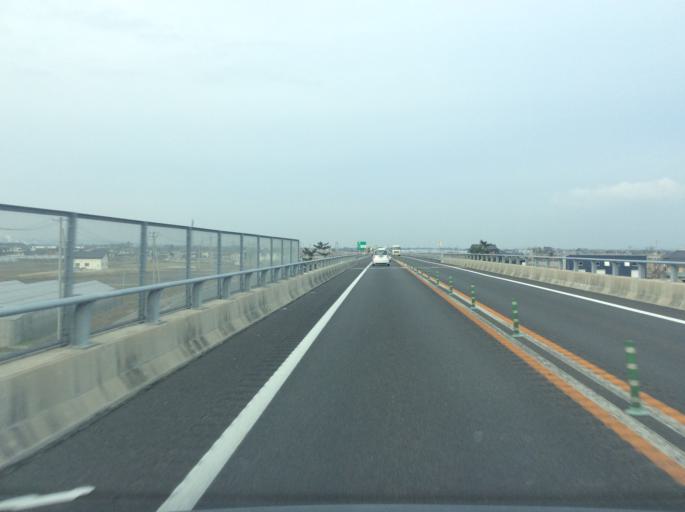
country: JP
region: Miyagi
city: Watari
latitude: 38.0272
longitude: 140.8901
